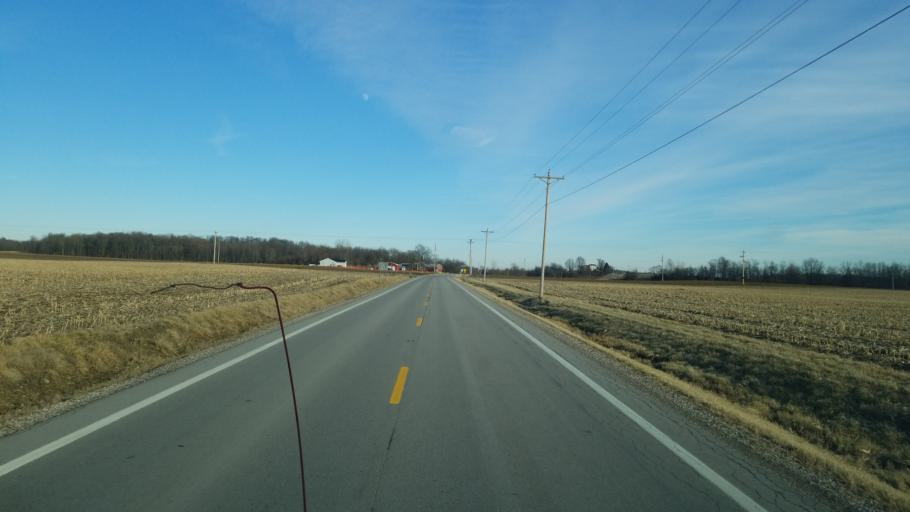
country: US
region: Ohio
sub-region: Huron County
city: Greenwich
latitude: 41.1030
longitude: -82.5399
